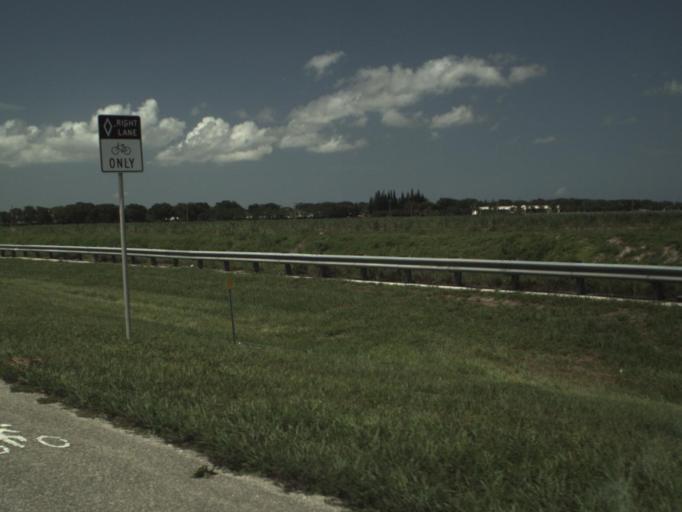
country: US
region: Florida
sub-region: Palm Beach County
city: Villages of Oriole
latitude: 26.4979
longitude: -80.2049
